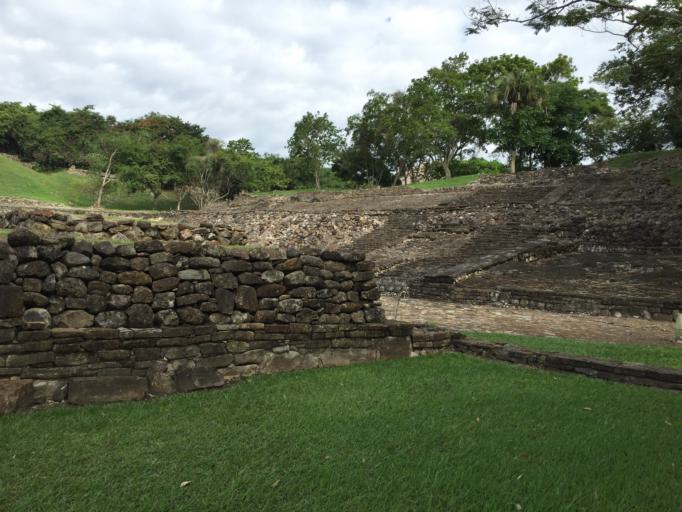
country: MX
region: Veracruz
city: Papantla de Olarte
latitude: 20.4484
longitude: -97.3770
